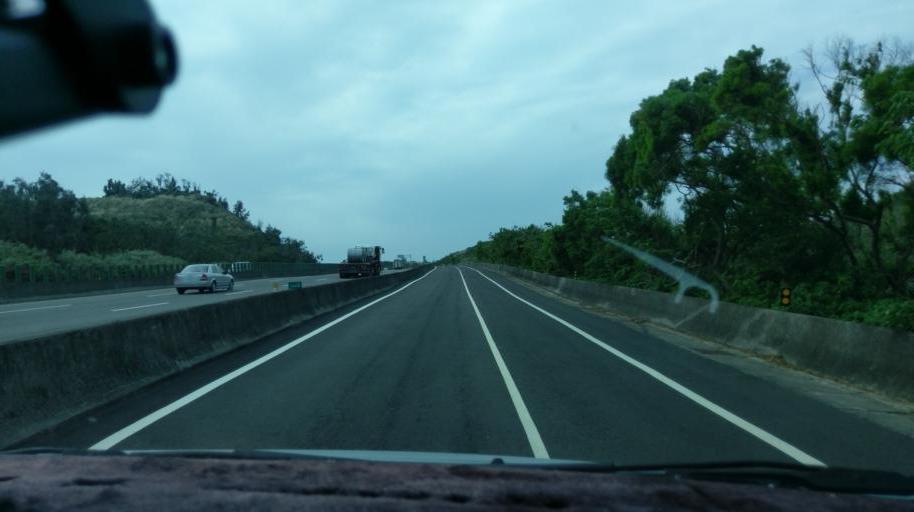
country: TW
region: Taiwan
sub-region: Miaoli
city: Miaoli
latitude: 24.5951
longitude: 120.7376
